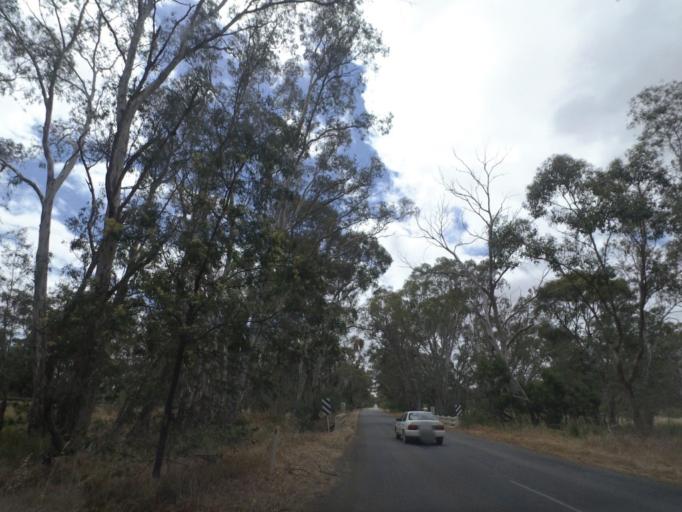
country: AU
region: Victoria
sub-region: Murrindindi
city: Kinglake West
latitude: -36.9325
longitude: 145.1808
